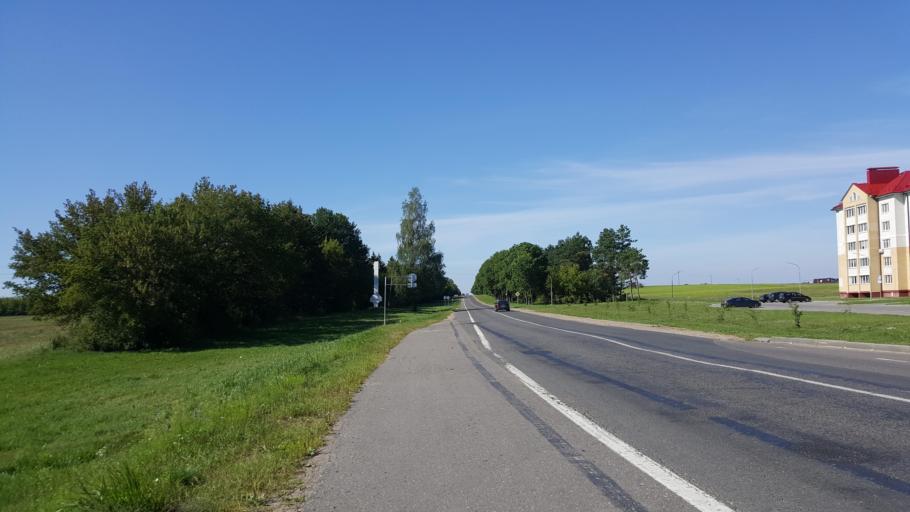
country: BY
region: Brest
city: Kamyanyets
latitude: 52.3885
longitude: 23.8189
